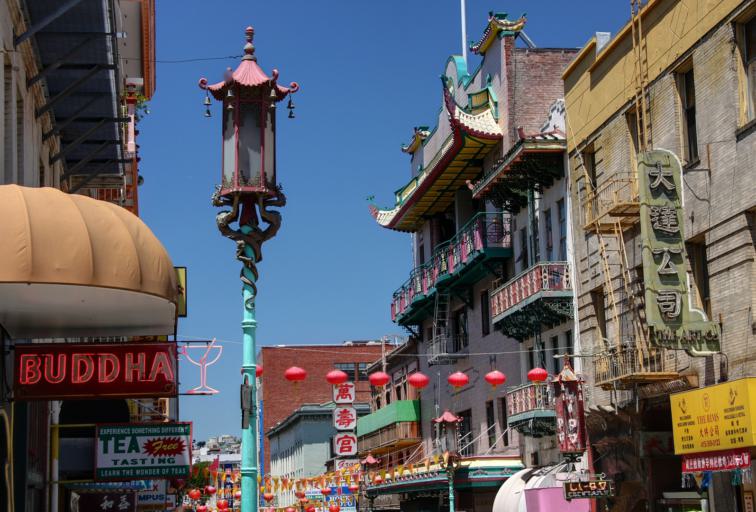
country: US
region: California
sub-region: San Francisco County
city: San Francisco
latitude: 37.7952
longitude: -122.4065
